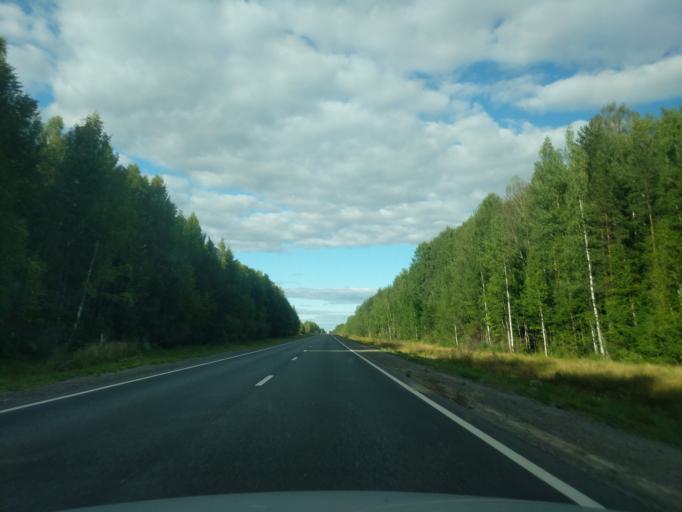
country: RU
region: Kostroma
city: Manturovo
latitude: 58.2247
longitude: 44.6240
